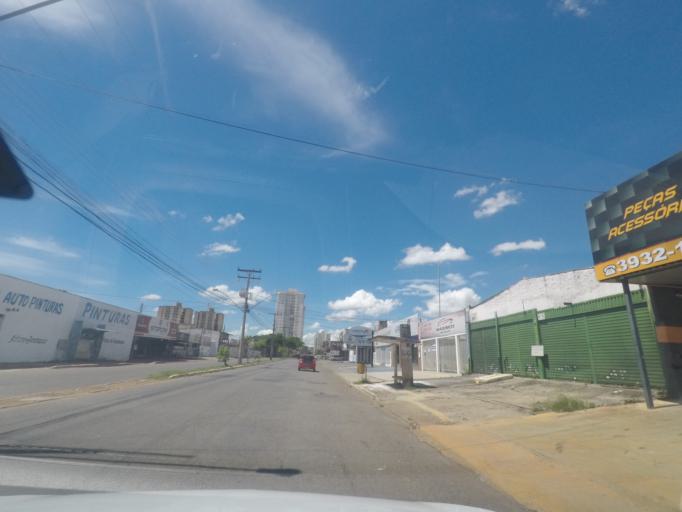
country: BR
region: Goias
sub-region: Goiania
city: Goiania
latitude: -16.6865
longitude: -49.2970
